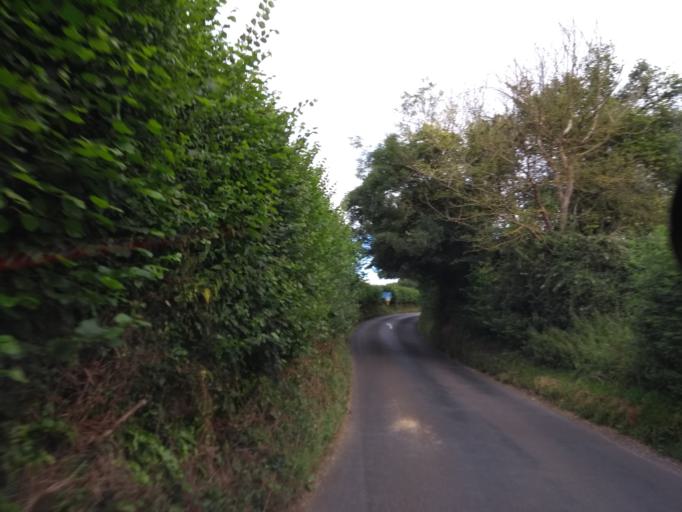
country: GB
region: England
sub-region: Somerset
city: Crewkerne
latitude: 50.8715
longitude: -2.7916
